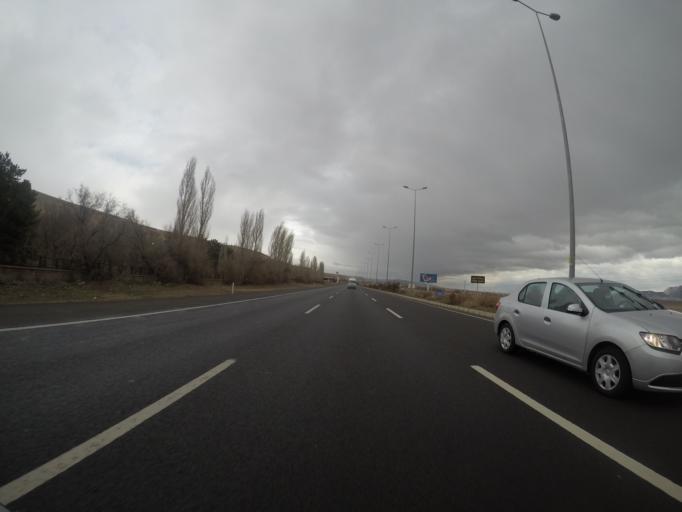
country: TR
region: Kayseri
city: Incesu
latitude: 38.7269
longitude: 35.2792
